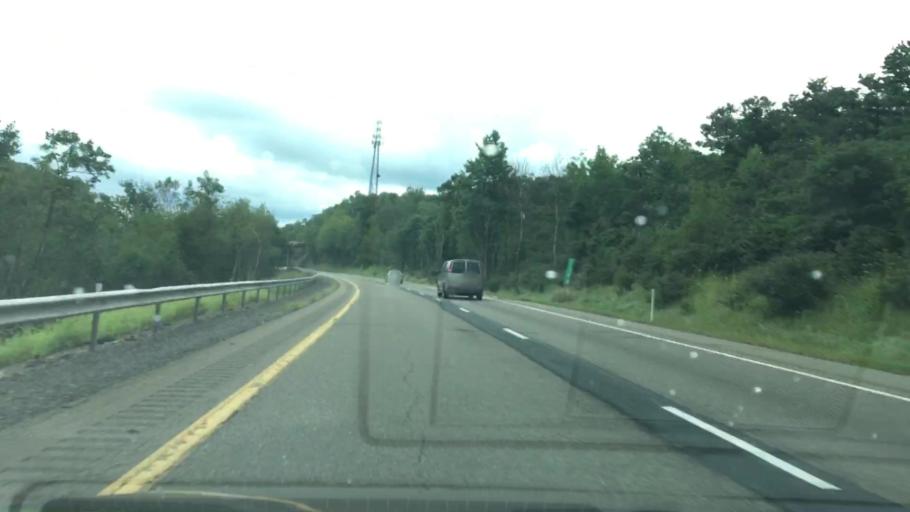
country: US
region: Pennsylvania
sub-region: Schuylkill County
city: Hometown
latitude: 40.8485
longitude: -76.0548
